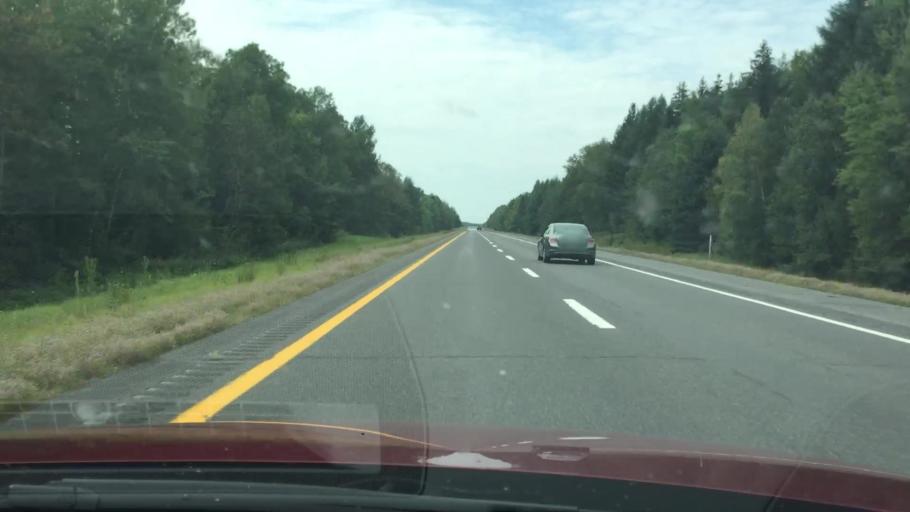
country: US
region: Maine
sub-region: Aroostook County
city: Houlton
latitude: 46.1371
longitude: -67.8778
